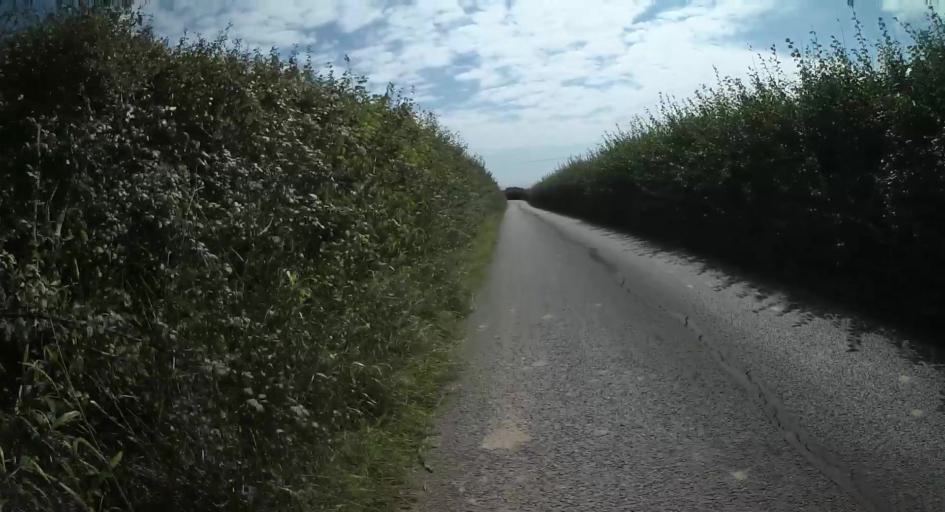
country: GB
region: England
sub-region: Isle of Wight
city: Chale
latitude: 50.6231
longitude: -1.3686
